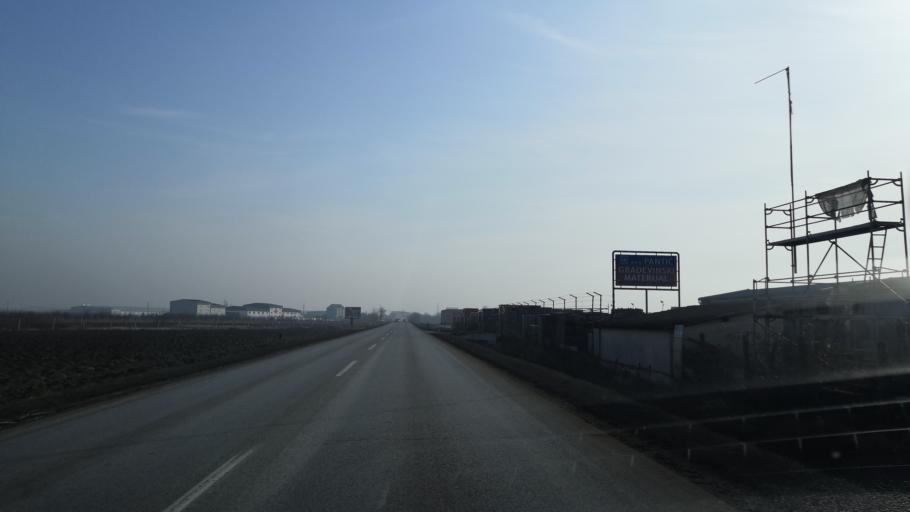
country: RS
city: Rumenka
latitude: 45.2871
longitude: 19.7582
